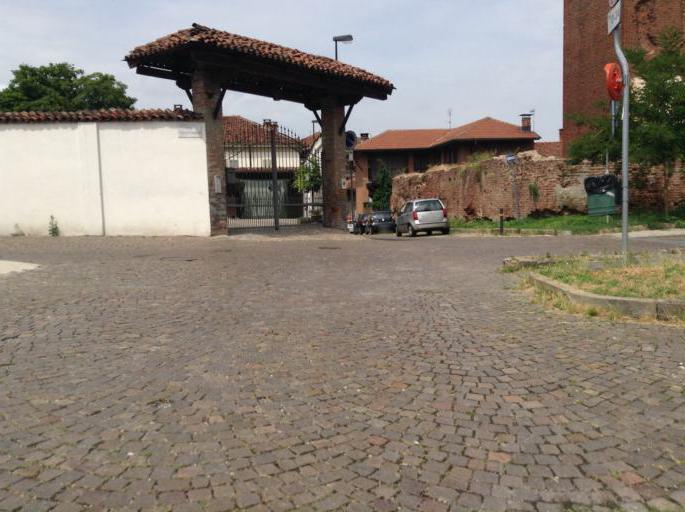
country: IT
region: Piedmont
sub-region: Provincia di Torino
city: Carignano
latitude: 44.9052
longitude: 7.6762
